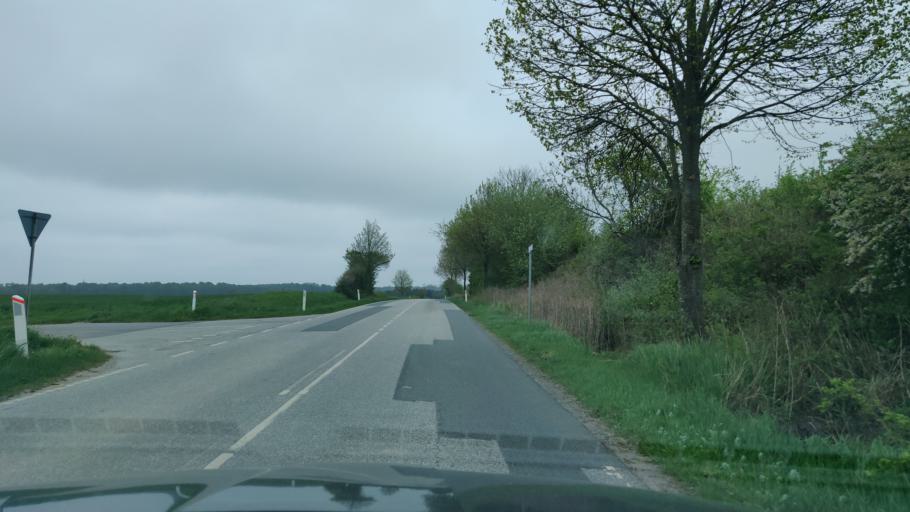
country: DK
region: South Denmark
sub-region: Sonderborg Kommune
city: Guderup
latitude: 54.9992
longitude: 9.9146
